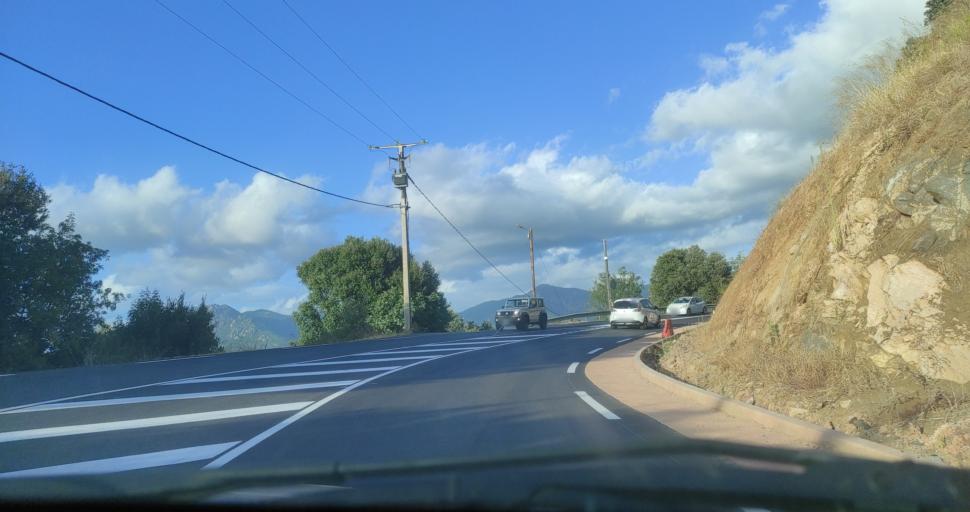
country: FR
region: Corsica
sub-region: Departement de la Corse-du-Sud
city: Appietto
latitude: 42.0347
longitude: 8.7634
